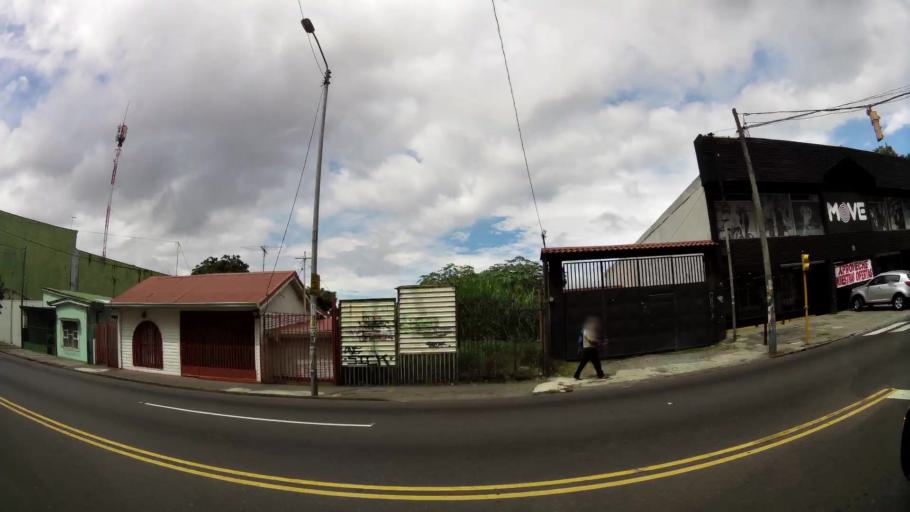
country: CR
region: San Jose
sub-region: Canton de Goicoechea
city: Guadalupe
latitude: 9.9443
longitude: -84.0579
